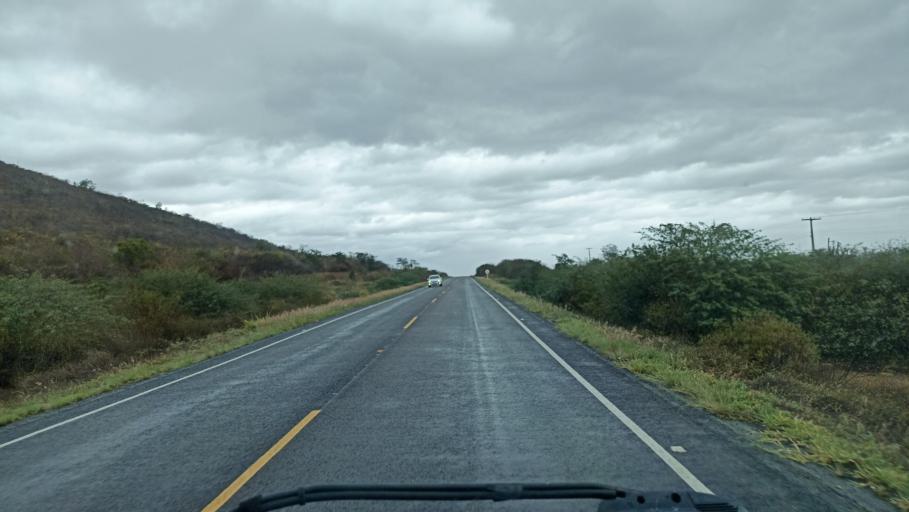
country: BR
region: Bahia
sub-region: Iacu
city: Iacu
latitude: -12.9586
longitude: -40.4733
